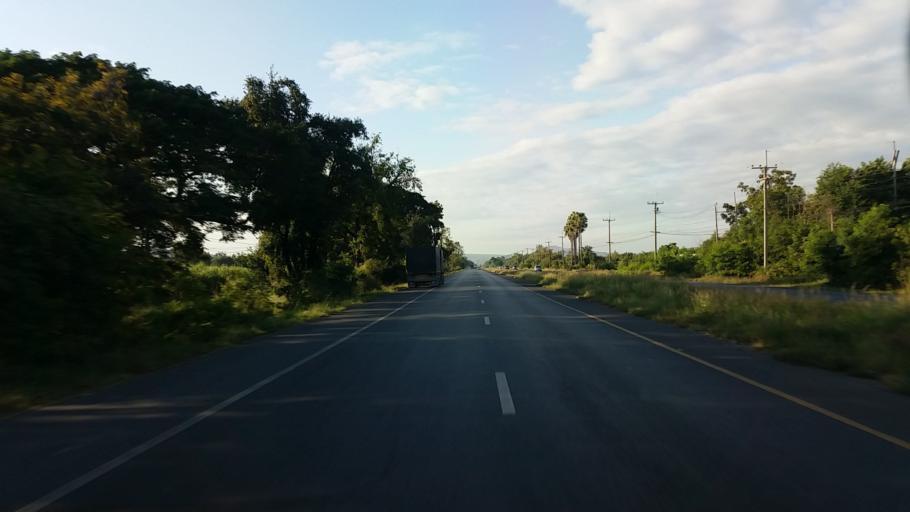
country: TH
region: Lop Buri
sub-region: Amphoe Tha Luang
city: Tha Luang
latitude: 15.0286
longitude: 100.9508
